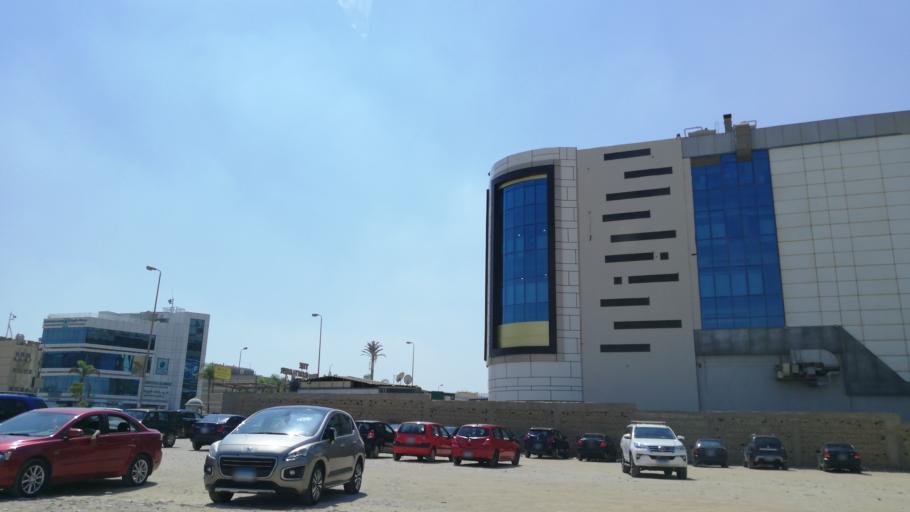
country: EG
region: Muhafazat al Qalyubiyah
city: Al Khankah
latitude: 30.0279
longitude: 31.4896
